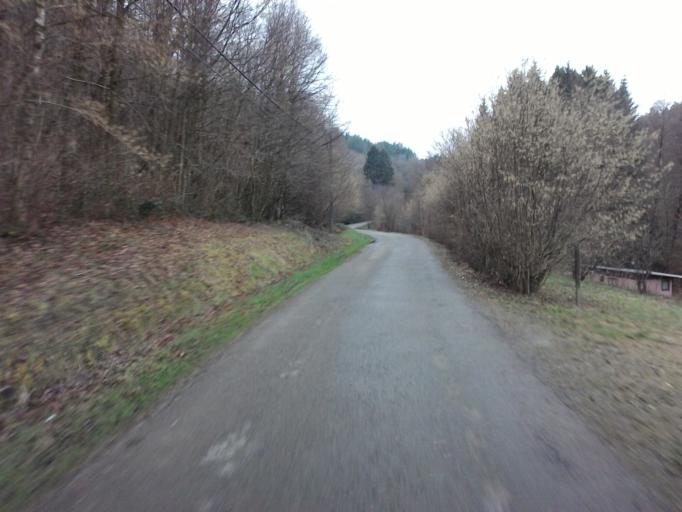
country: BE
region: Wallonia
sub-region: Province de Namur
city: Gedinne
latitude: 50.0291
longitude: 4.8853
